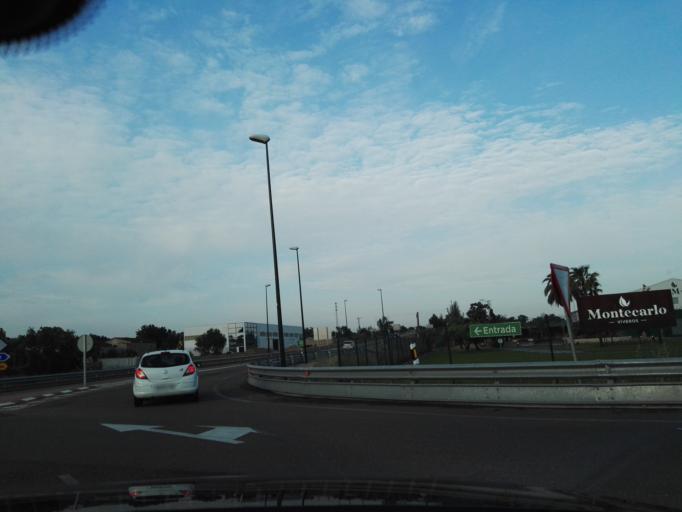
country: ES
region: Aragon
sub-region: Provincia de Zaragoza
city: Utebo
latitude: 41.6645
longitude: -0.9991
